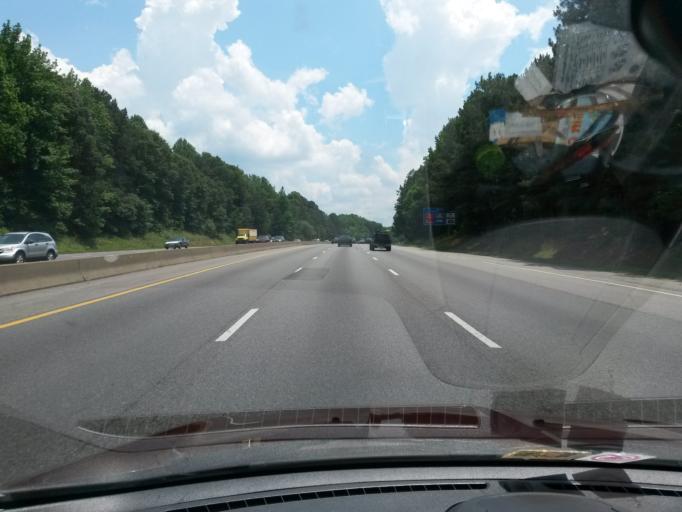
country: US
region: Virginia
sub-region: Chesterfield County
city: Chester
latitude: 37.3738
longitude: -77.4060
